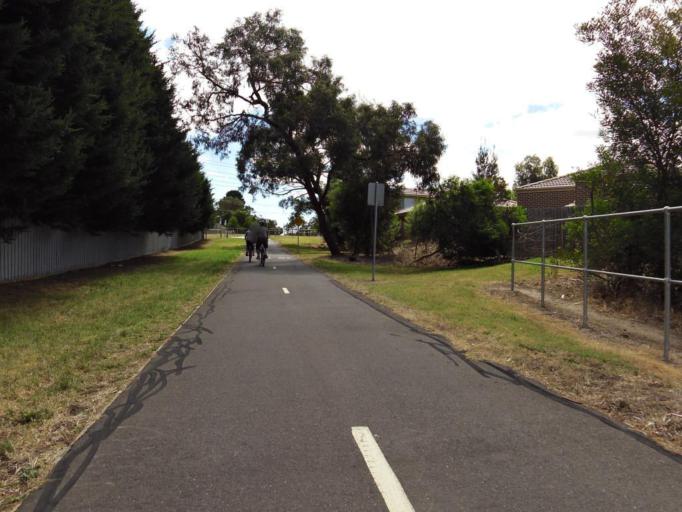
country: AU
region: Victoria
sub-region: Frankston
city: Langwarrin
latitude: -38.1616
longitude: 145.1624
